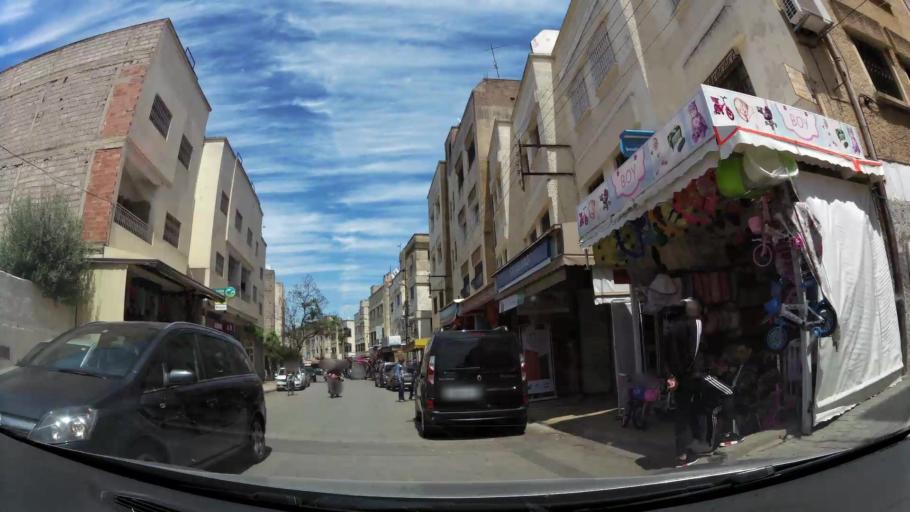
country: MA
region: Fes-Boulemane
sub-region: Fes
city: Fes
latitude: 34.0116
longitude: -4.9878
